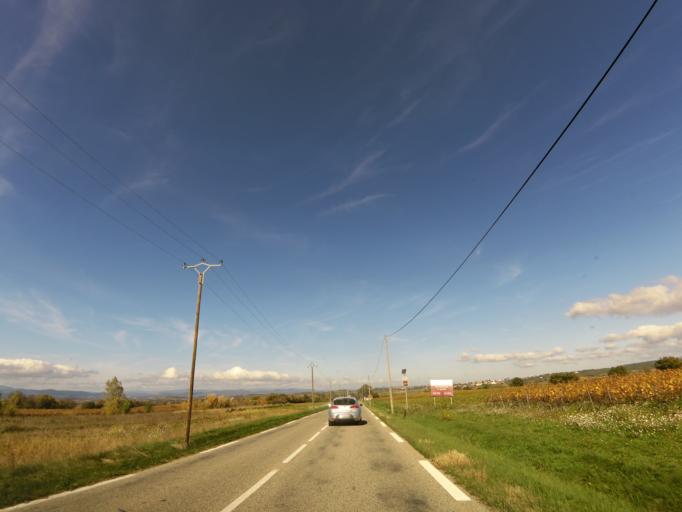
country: FR
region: Languedoc-Roussillon
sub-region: Departement du Gard
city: Ledignan
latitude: 43.9578
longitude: 4.0991
